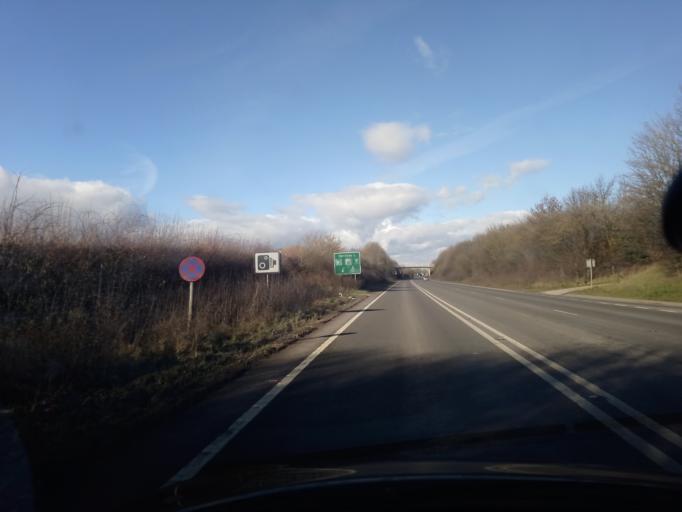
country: GB
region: England
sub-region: Shropshire
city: Whitchurch
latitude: 52.9611
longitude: -2.6995
